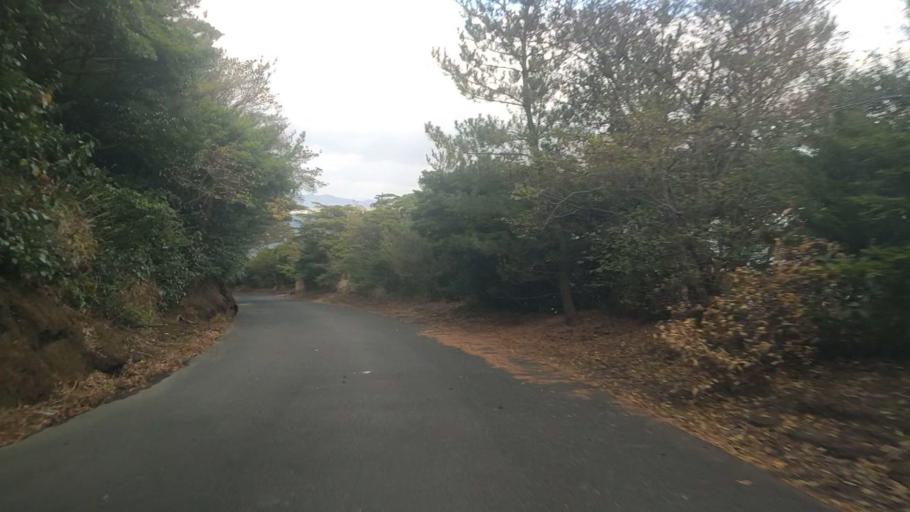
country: JP
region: Kagoshima
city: Kagoshima-shi
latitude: 31.5941
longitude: 130.6350
